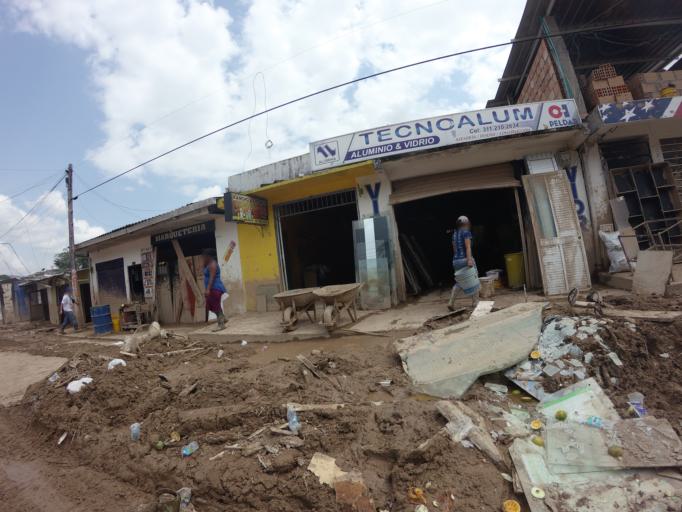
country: CO
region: Putumayo
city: Mocoa
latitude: 1.1500
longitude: -76.6496
